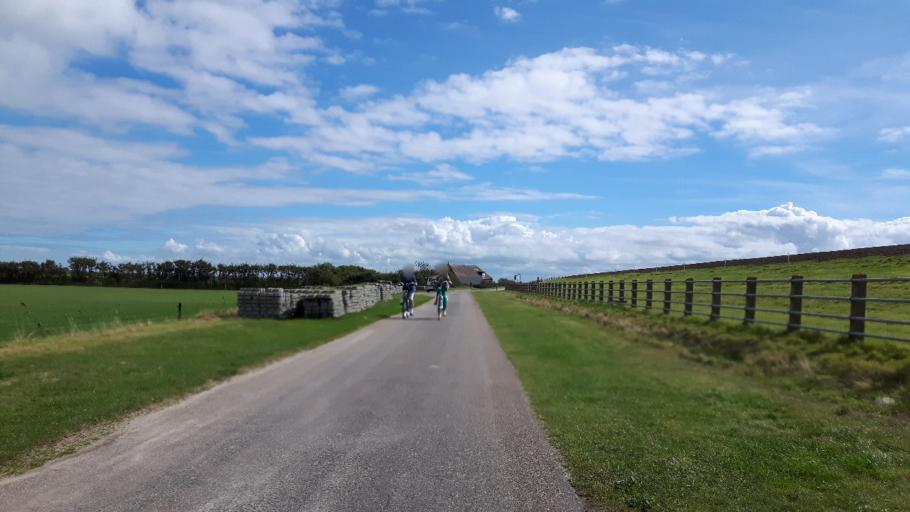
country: NL
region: Friesland
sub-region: Gemeente Ameland
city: Hollum
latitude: 53.4350
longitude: 5.6275
